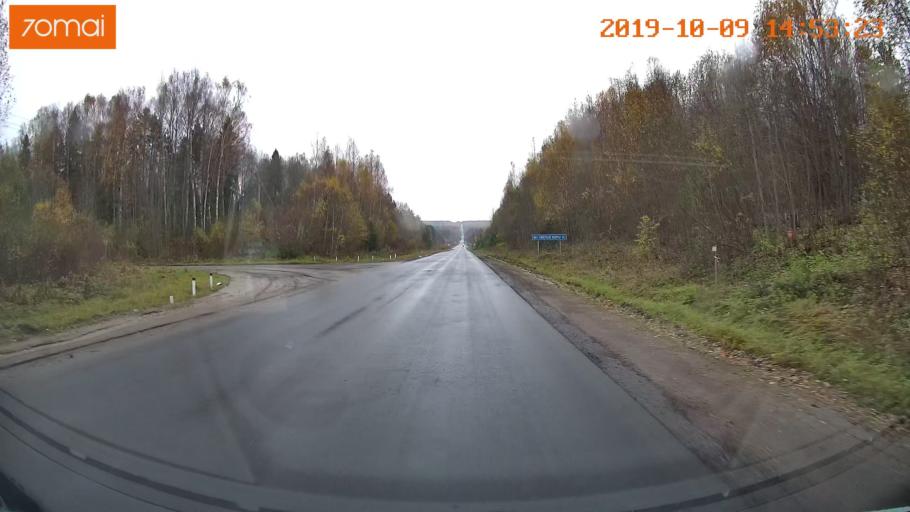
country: RU
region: Kostroma
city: Chistyye Bory
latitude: 58.3683
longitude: 41.6381
